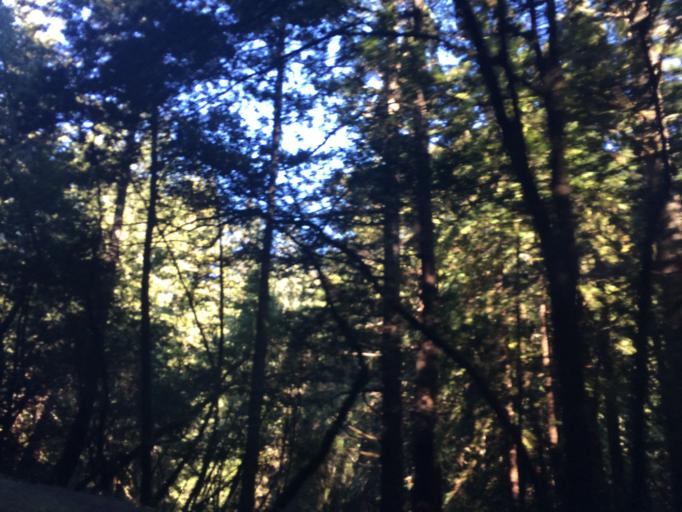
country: US
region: California
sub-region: Marin County
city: Lagunitas-Forest Knolls
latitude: 38.0140
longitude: -122.7163
